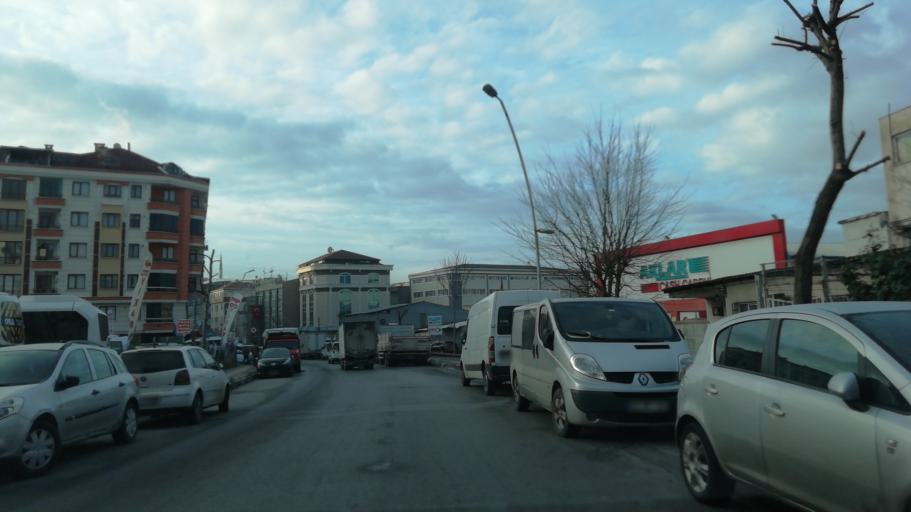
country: TR
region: Istanbul
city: Bahcelievler
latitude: 41.0043
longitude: 28.8266
